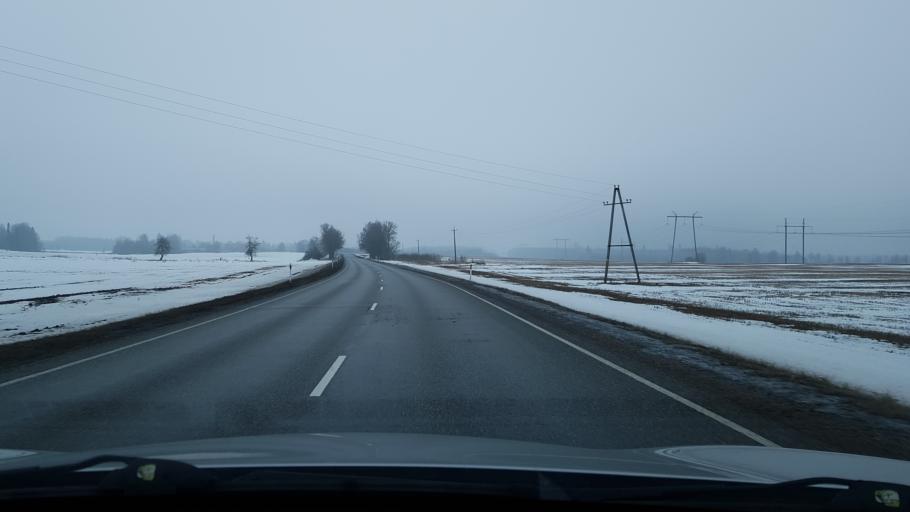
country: EE
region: Valgamaa
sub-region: Valga linn
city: Valga
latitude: 57.9402
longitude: 26.1686
